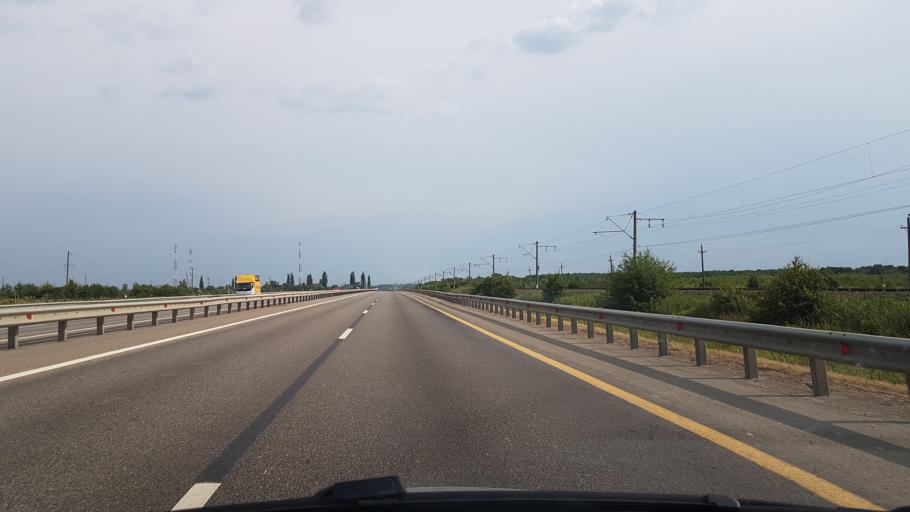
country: RU
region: Adygeya
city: Adygeysk
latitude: 44.8127
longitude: 39.2278
